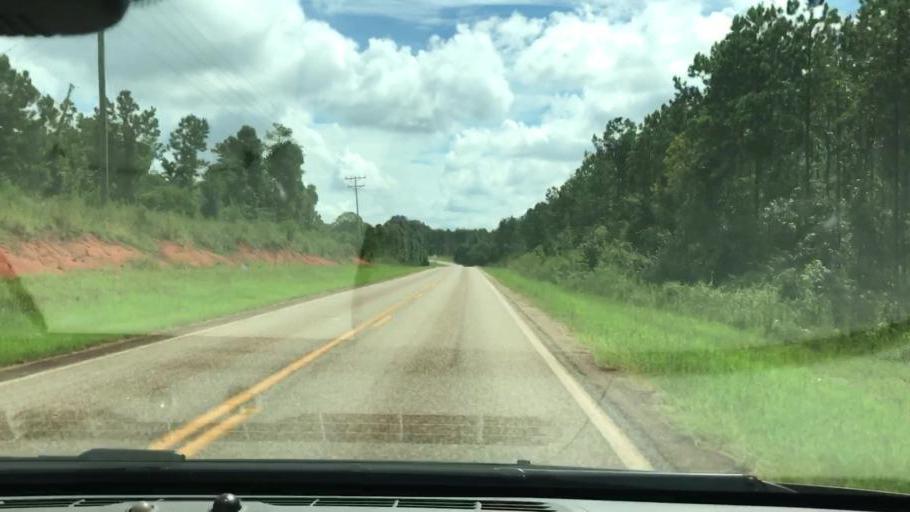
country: US
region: Georgia
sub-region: Stewart County
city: Lumpkin
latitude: 32.0670
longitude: -84.9018
